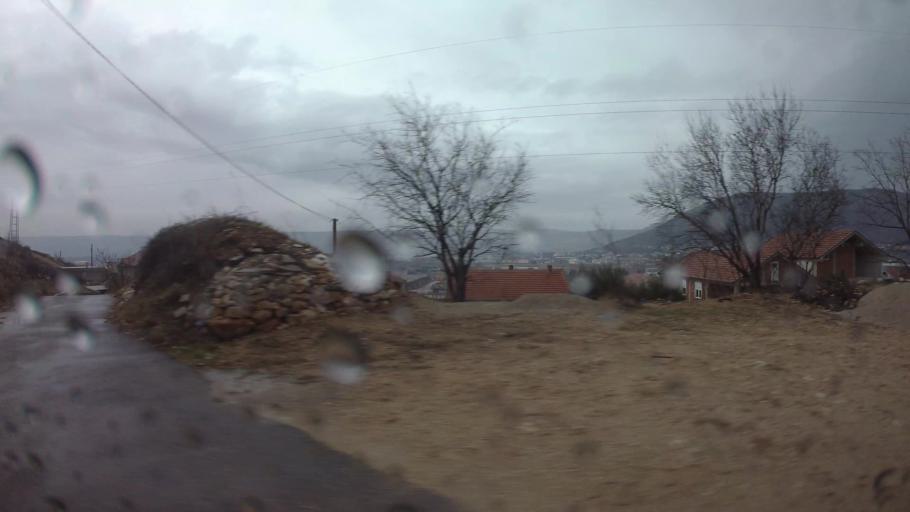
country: BA
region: Federation of Bosnia and Herzegovina
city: Rodoc
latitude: 43.3141
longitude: 17.8376
